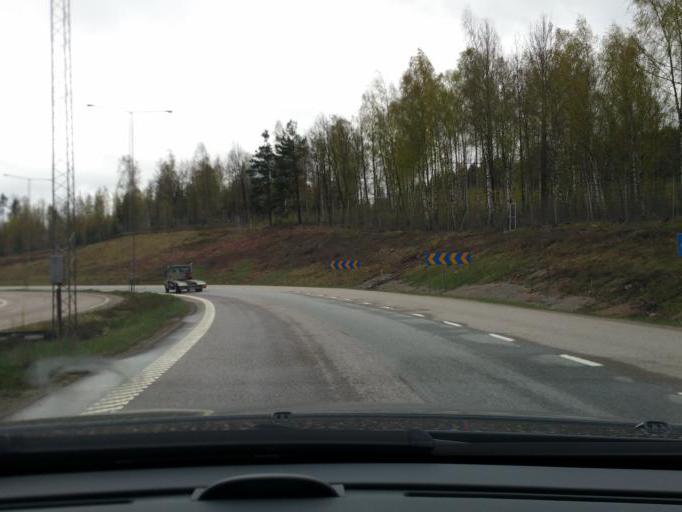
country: SE
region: Kronoberg
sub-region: Vaxjo Kommun
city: Vaexjoe
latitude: 56.8972
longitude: 14.7283
